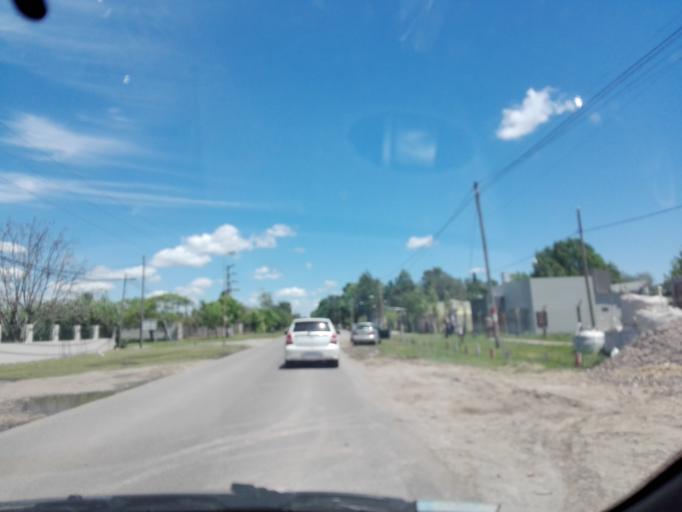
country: AR
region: Buenos Aires
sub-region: Partido de La Plata
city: La Plata
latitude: -34.8977
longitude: -58.0152
